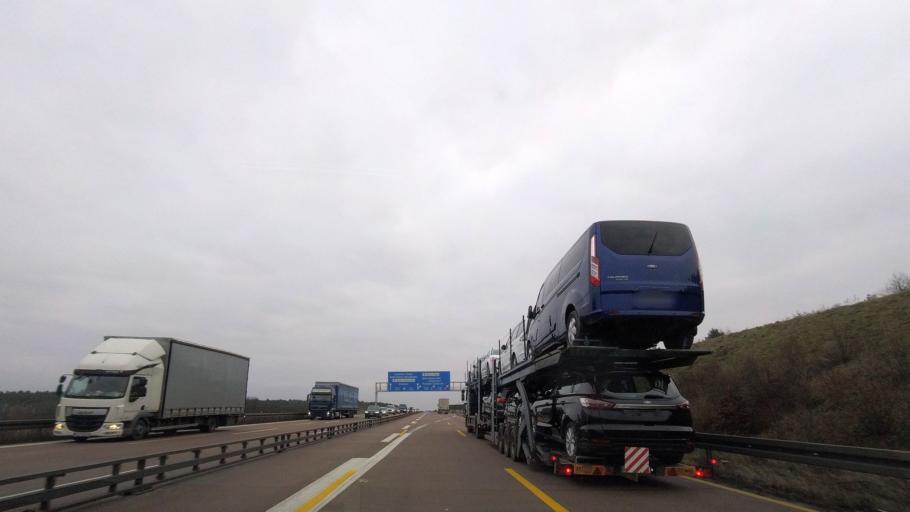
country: DE
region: Brandenburg
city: Michendorf
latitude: 52.3008
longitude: 13.0560
